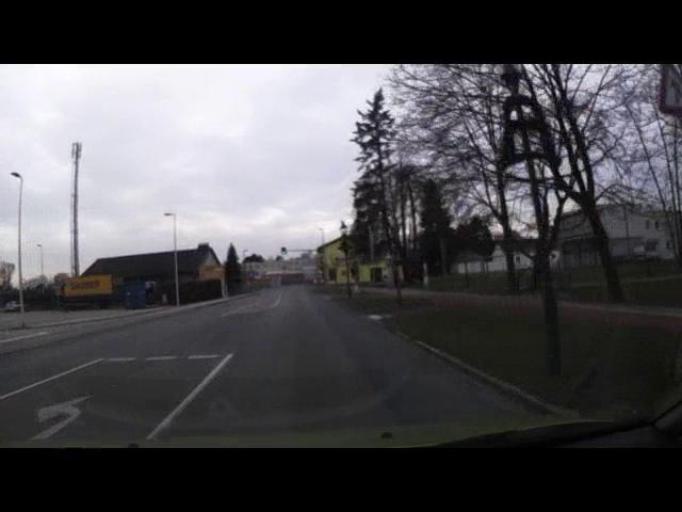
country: AT
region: Lower Austria
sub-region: Politischer Bezirk Wiener Neustadt
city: Ebenfurth
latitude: 47.8748
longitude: 16.3748
